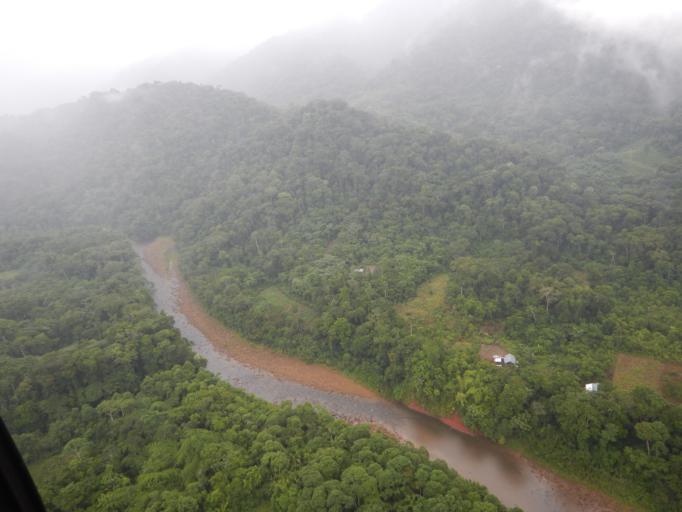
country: BO
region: Santa Cruz
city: Comarapa
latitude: -17.3172
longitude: -64.5488
